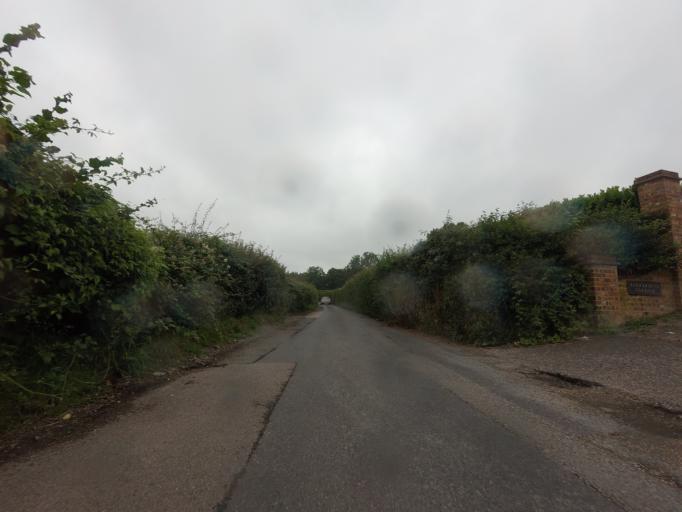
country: GB
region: England
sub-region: Kent
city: Kemsing
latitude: 51.3110
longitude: 0.2422
